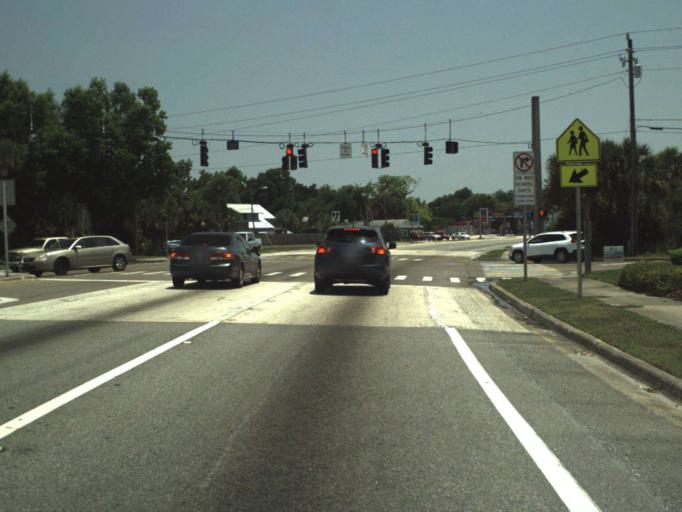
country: US
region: Florida
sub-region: Volusia County
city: Edgewater
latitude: 29.0051
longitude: -80.9151
